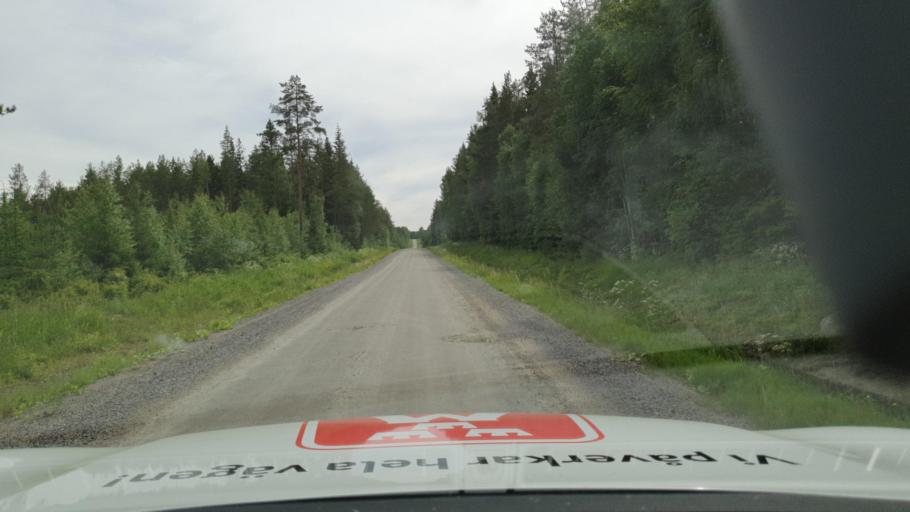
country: SE
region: Vaesterbotten
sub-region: Skelleftea Kommun
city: Burea
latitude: 64.4534
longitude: 21.0277
